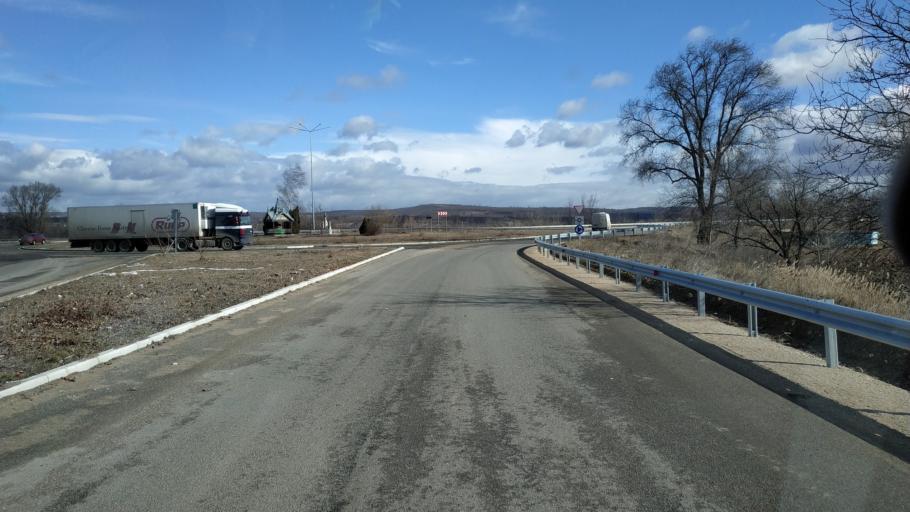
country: MD
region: Stinga Nistrului
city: Bucovat
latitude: 47.1798
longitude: 28.4664
